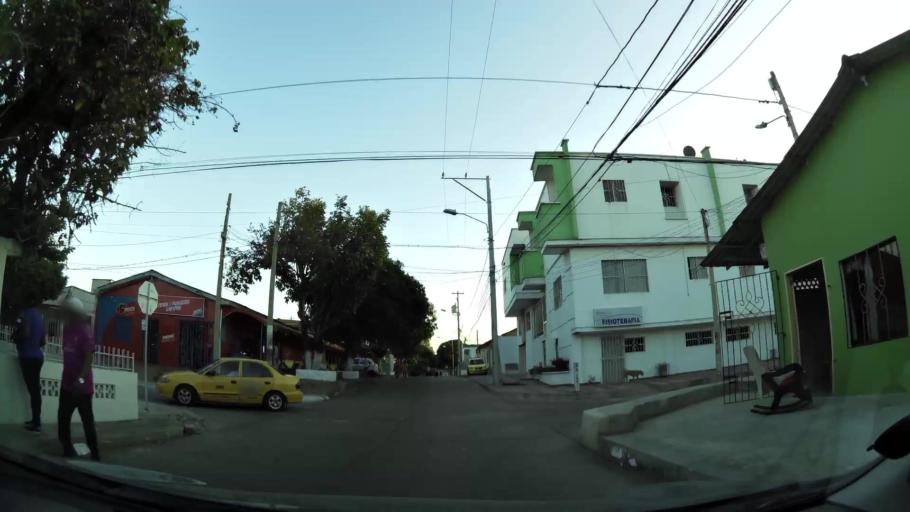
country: CO
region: Atlantico
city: Barranquilla
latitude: 10.9748
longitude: -74.8064
